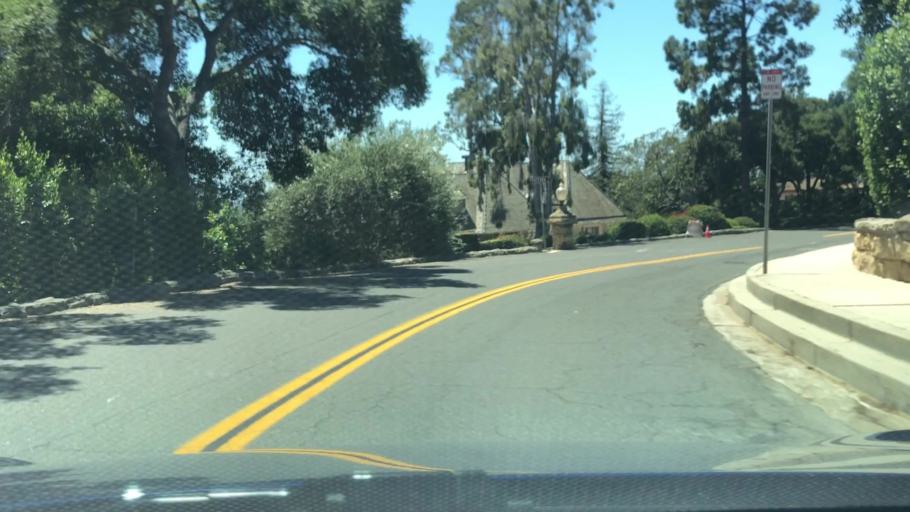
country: US
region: California
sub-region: Santa Barbara County
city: Mission Canyon
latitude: 34.4384
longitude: -119.7019
